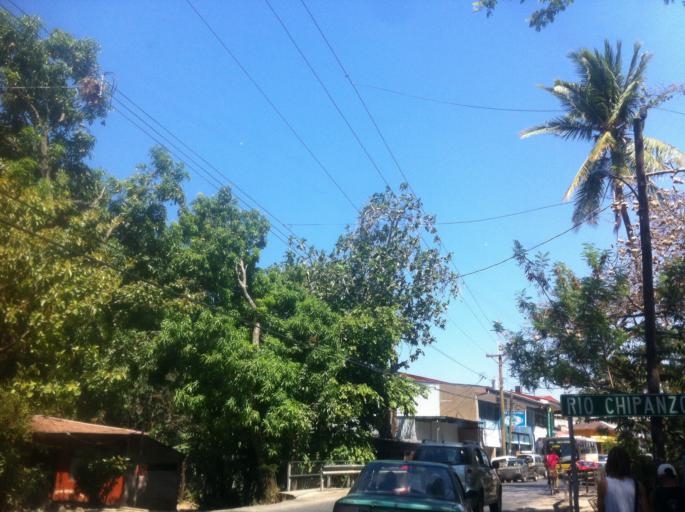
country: CR
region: Guanacaste
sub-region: Canton de Nicoya
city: Nicoya
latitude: 10.1322
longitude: -85.4439
